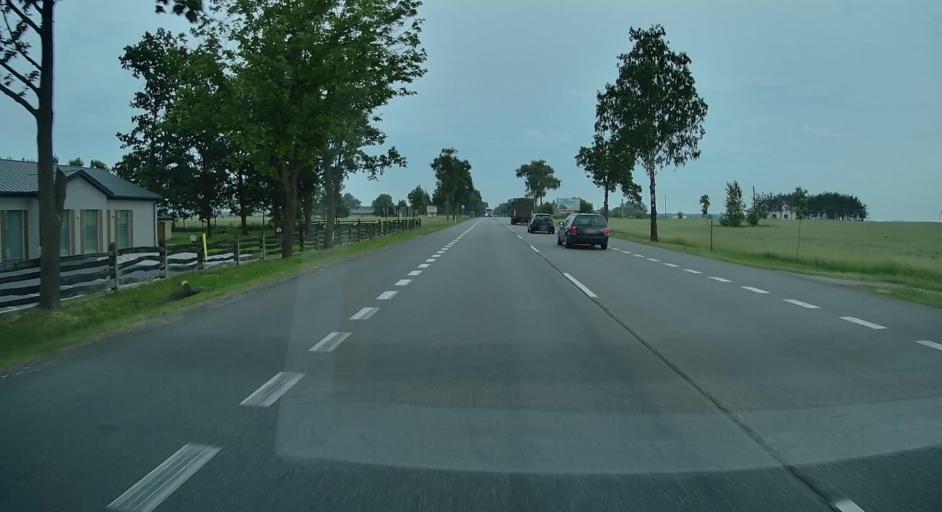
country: PL
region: Masovian Voivodeship
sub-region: Powiat siedlecki
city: Zbuczyn
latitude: 52.1166
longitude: 22.3664
